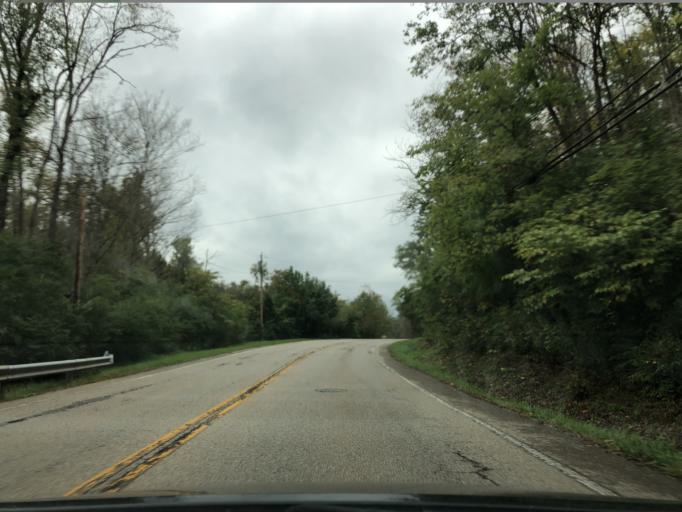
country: US
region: Ohio
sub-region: Hamilton County
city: Madeira
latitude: 39.1745
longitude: -84.3767
